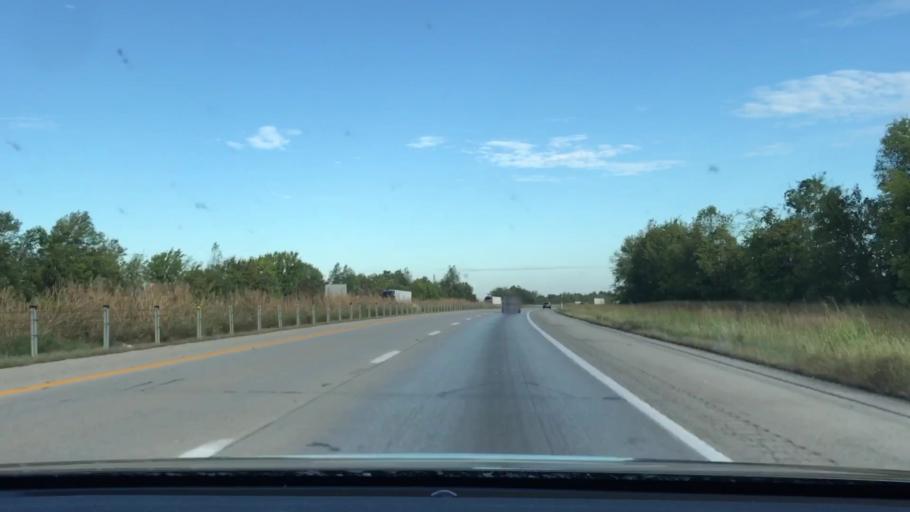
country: US
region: Kentucky
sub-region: Christian County
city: Oak Grove
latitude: 36.7146
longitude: -87.4810
